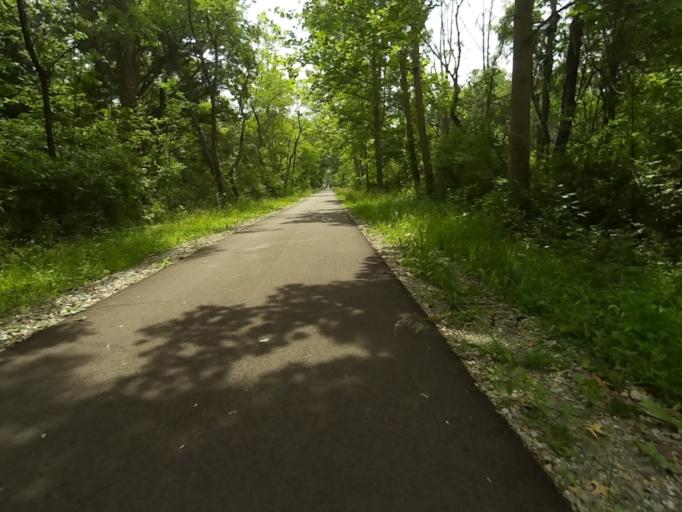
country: US
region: Ohio
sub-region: Summit County
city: Boston Heights
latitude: 41.2365
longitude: -81.5016
